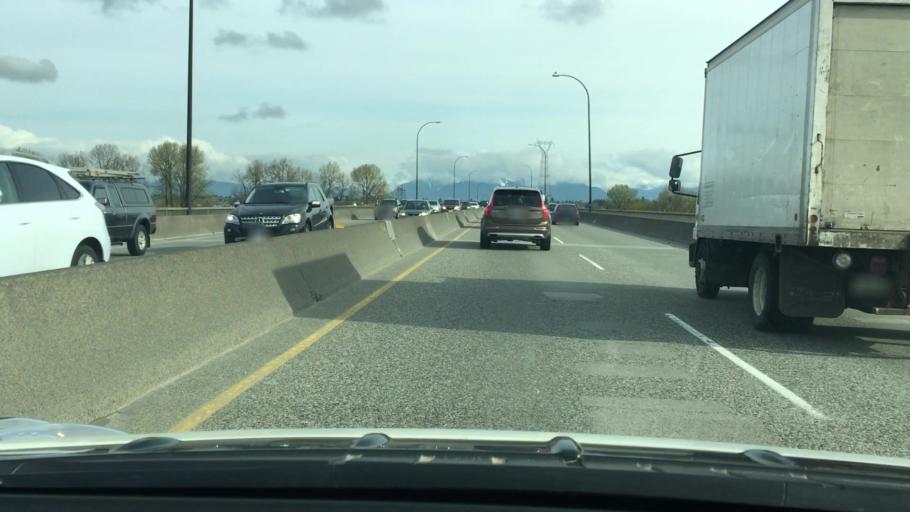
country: CA
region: British Columbia
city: Richmond
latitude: 49.1977
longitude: -123.0774
